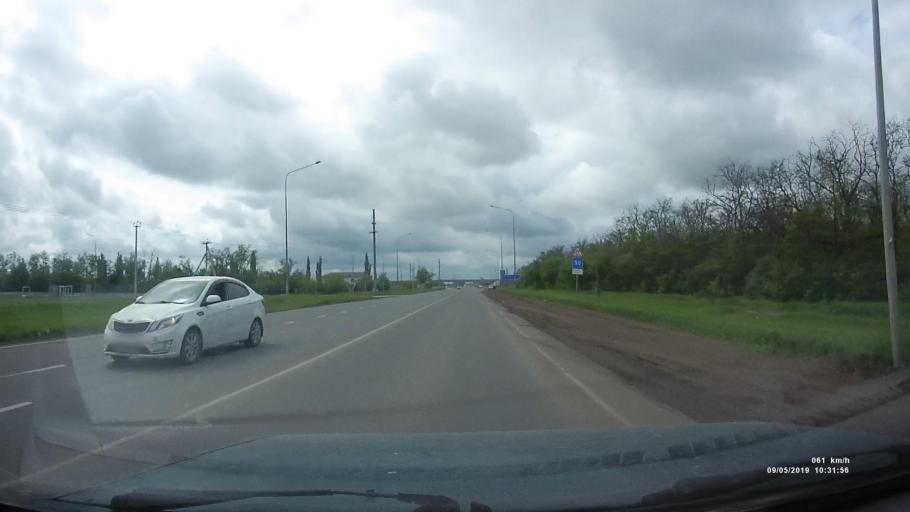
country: RU
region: Rostov
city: Azov
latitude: 47.0771
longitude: 39.4272
